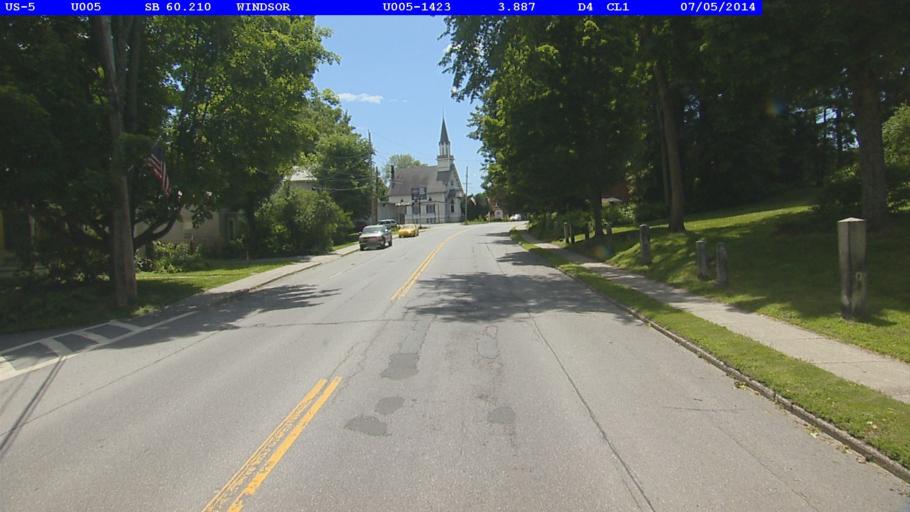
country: US
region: Vermont
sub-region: Windsor County
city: Windsor
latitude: 43.4826
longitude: -72.3854
